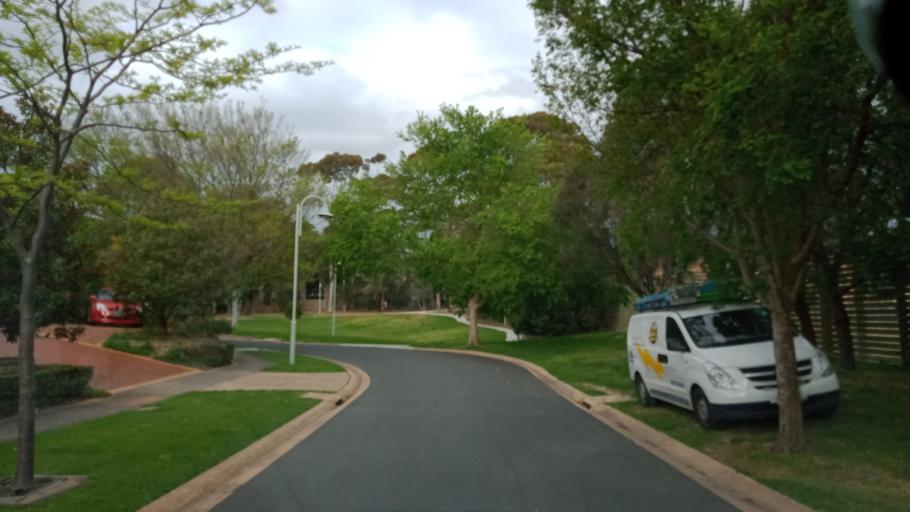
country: AU
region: Victoria
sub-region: Monash
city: Notting Hill
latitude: -37.8822
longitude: 145.1529
